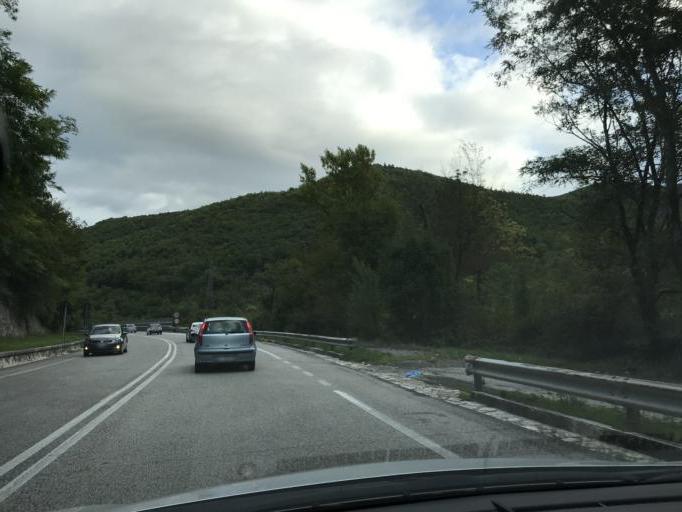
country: IT
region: Umbria
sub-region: Provincia di Perugia
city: Spoleto
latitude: 42.6807
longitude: 12.7265
